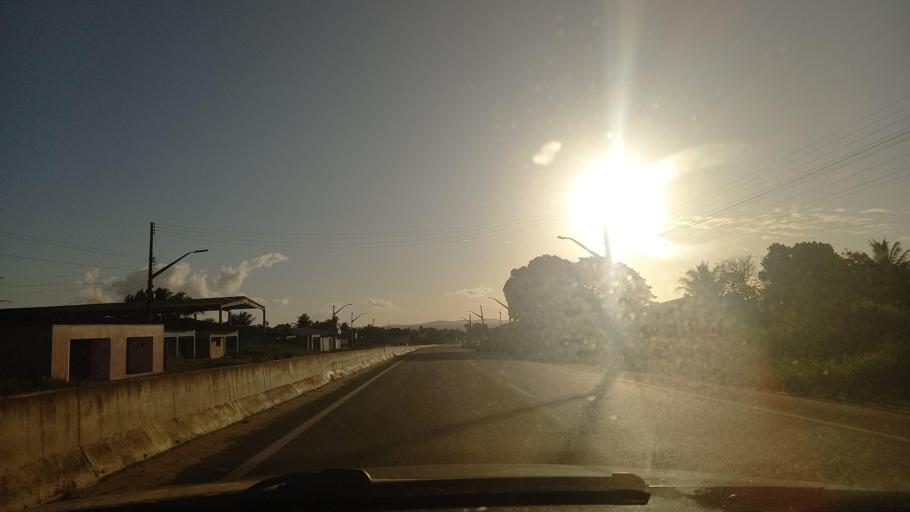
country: BR
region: Alagoas
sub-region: Limoeiro De Anadia
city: Limoeiro de Anadia
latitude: -9.7423
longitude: -36.4713
